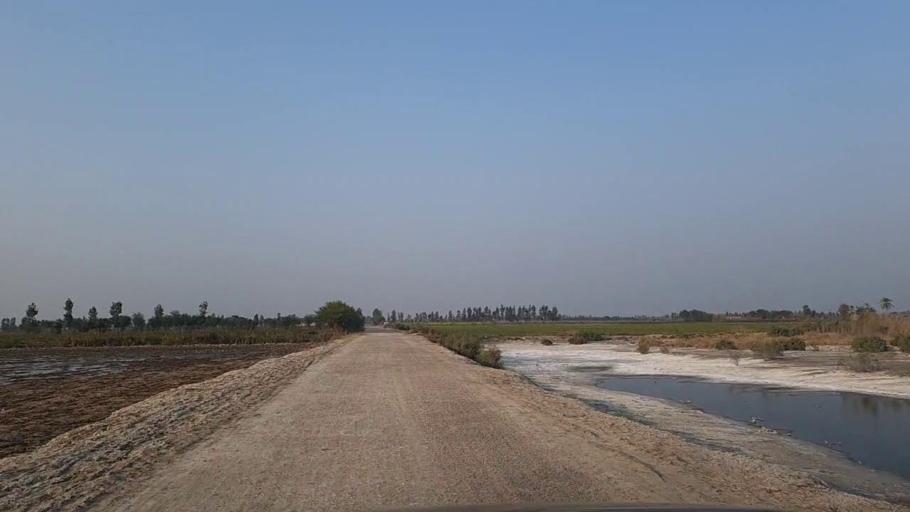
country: PK
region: Sindh
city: Daur
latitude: 26.4177
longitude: 68.3934
